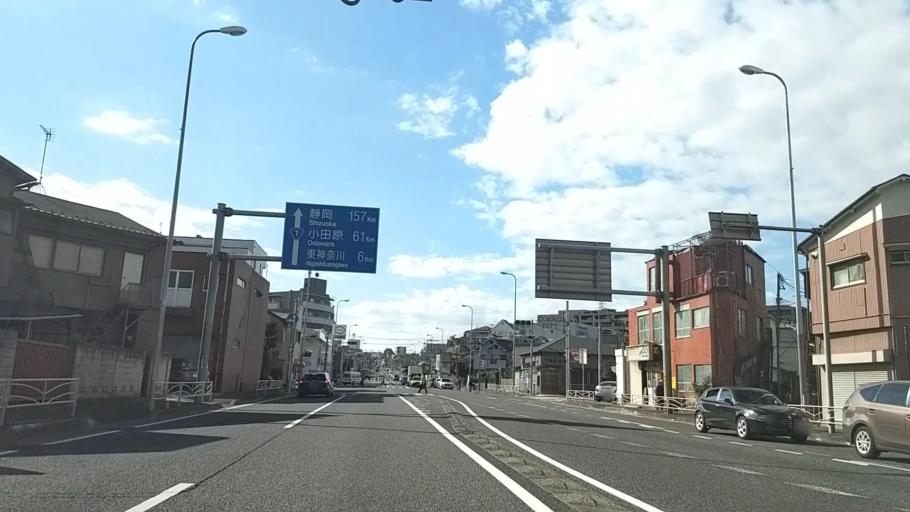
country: JP
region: Kanagawa
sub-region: Kawasaki-shi
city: Kawasaki
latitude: 35.5209
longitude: 139.6715
